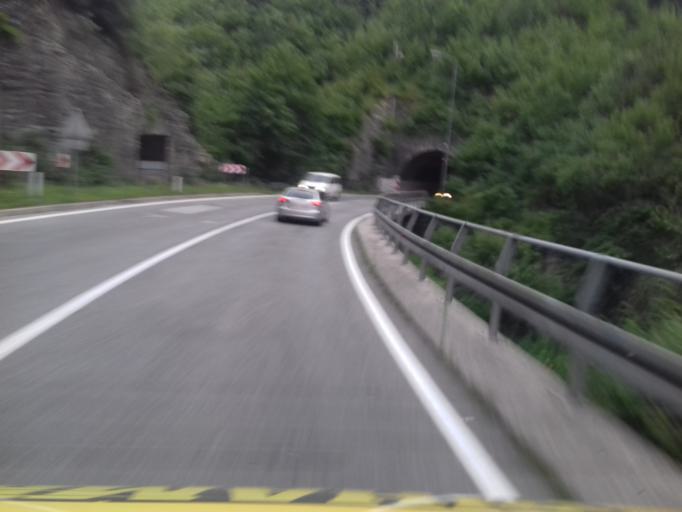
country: BA
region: Federation of Bosnia and Herzegovina
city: Jablanica
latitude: 43.6750
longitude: 17.7775
